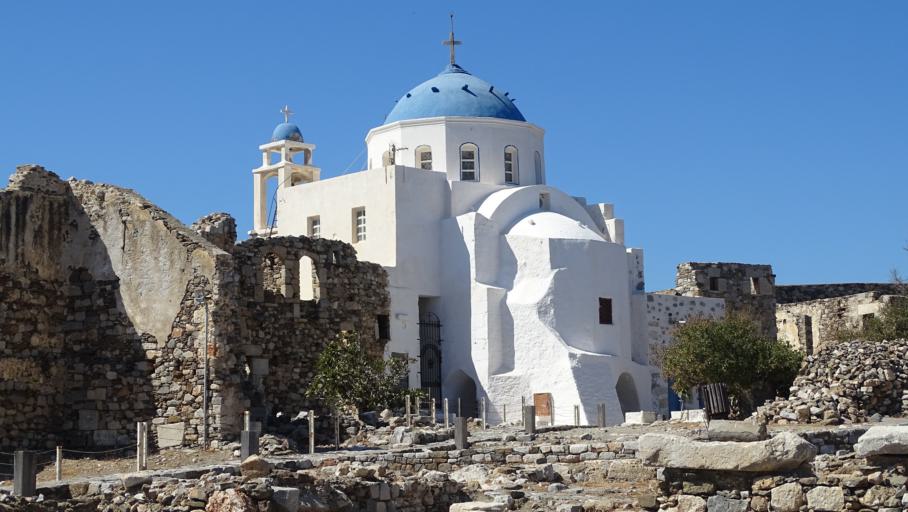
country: GR
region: South Aegean
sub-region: Nomos Dodekanisou
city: Astypalaia
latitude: 36.5440
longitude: 26.3555
